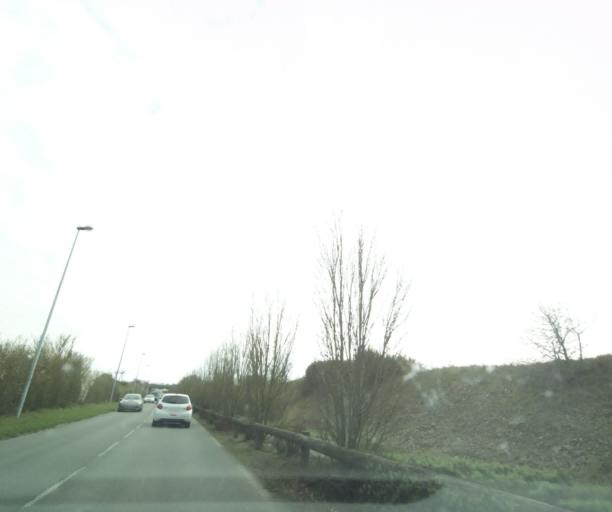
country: FR
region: Poitou-Charentes
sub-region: Departement de la Charente-Maritime
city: Lagord
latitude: 46.1782
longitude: -1.1676
